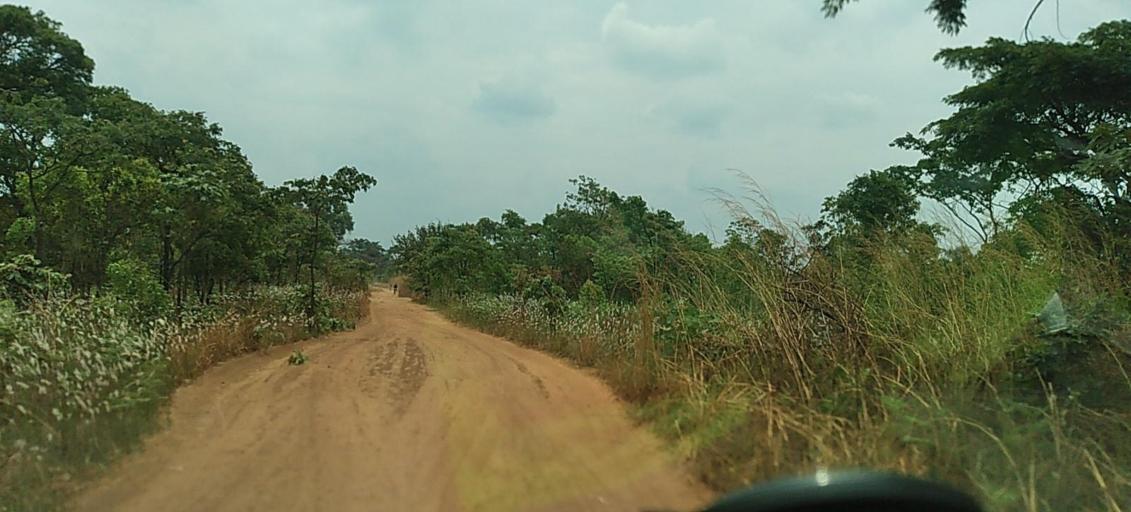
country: ZM
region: North-Western
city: Kansanshi
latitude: -12.0639
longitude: 26.3518
